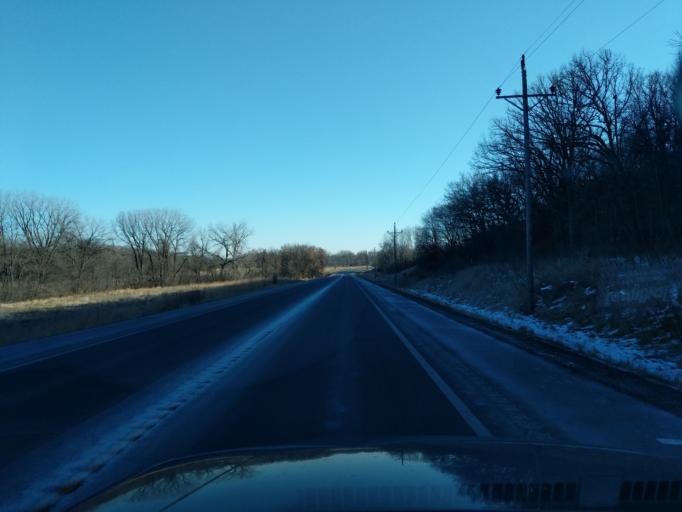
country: US
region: Minnesota
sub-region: Yellow Medicine County
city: Granite Falls
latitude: 44.8547
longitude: -95.6246
